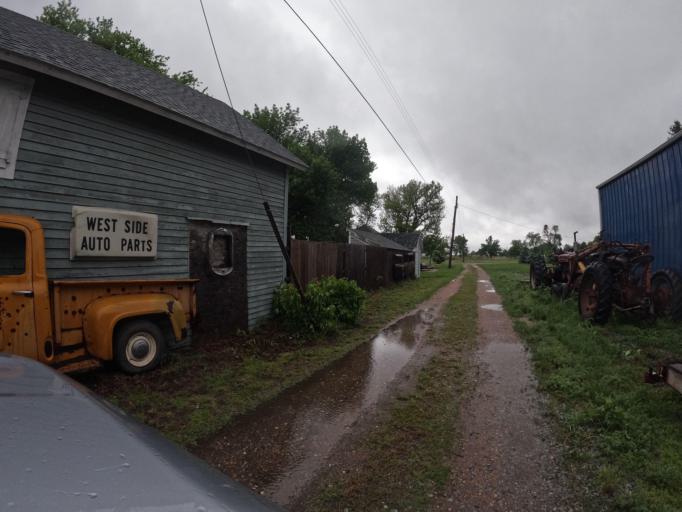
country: US
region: Nebraska
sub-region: Clay County
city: Harvard
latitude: 40.6211
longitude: -98.1006
